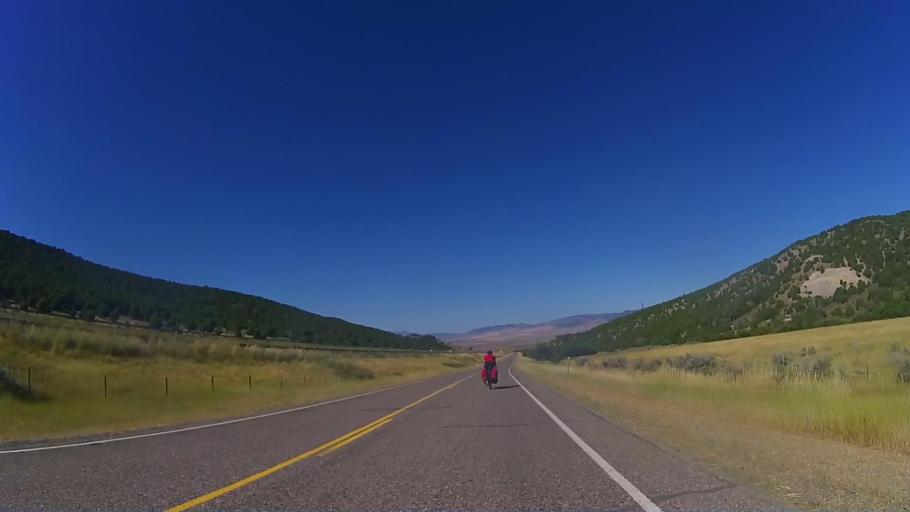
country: US
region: Idaho
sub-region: Oneida County
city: Malad City
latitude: 42.3568
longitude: -112.2201
